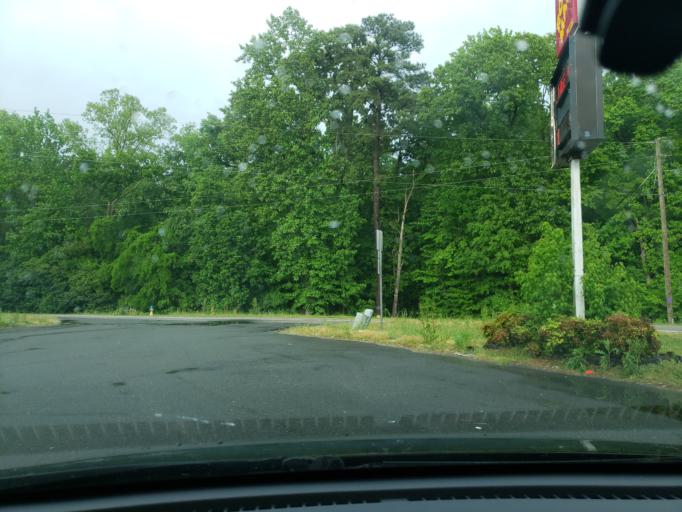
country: US
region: North Carolina
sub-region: Vance County
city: Henderson
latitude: 36.4068
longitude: -78.3693
